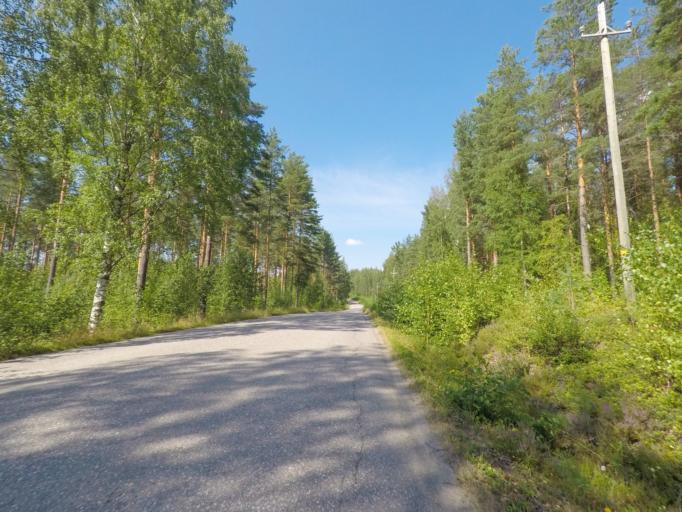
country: FI
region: Southern Savonia
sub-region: Mikkeli
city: Puumala
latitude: 61.4399
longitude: 28.1658
